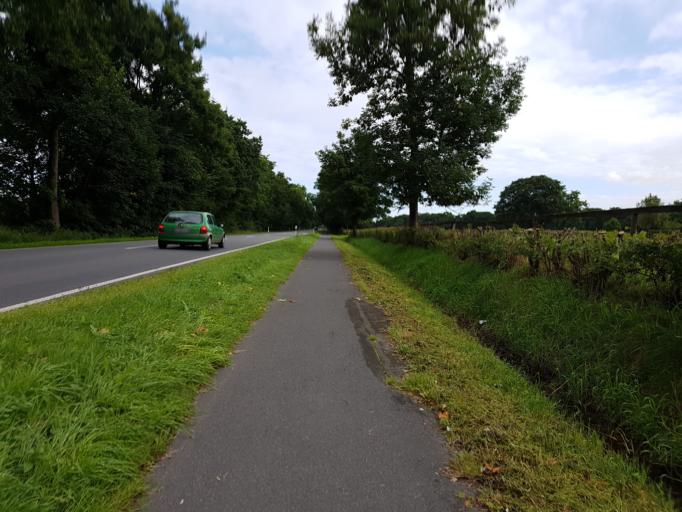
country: DE
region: Lower Saxony
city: Wittmund
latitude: 53.5547
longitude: 7.7839
